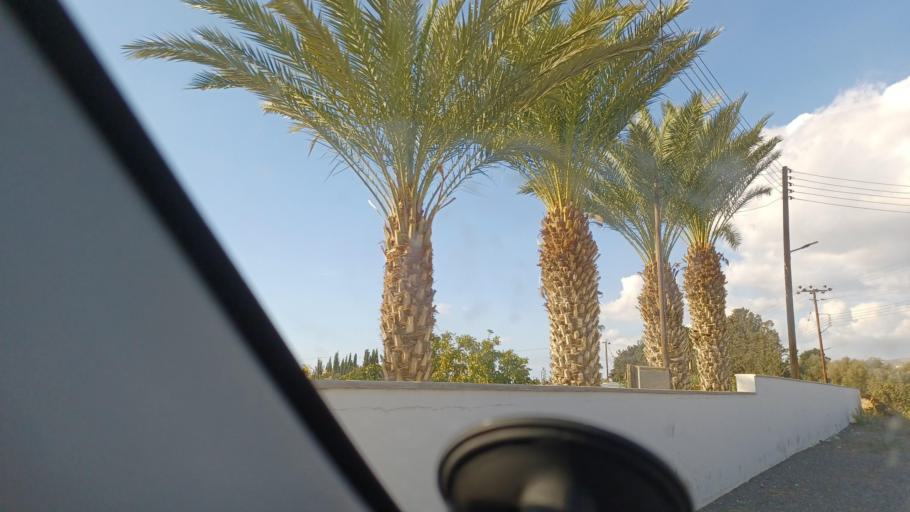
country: CY
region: Pafos
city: Mesogi
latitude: 34.7334
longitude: 32.5415
